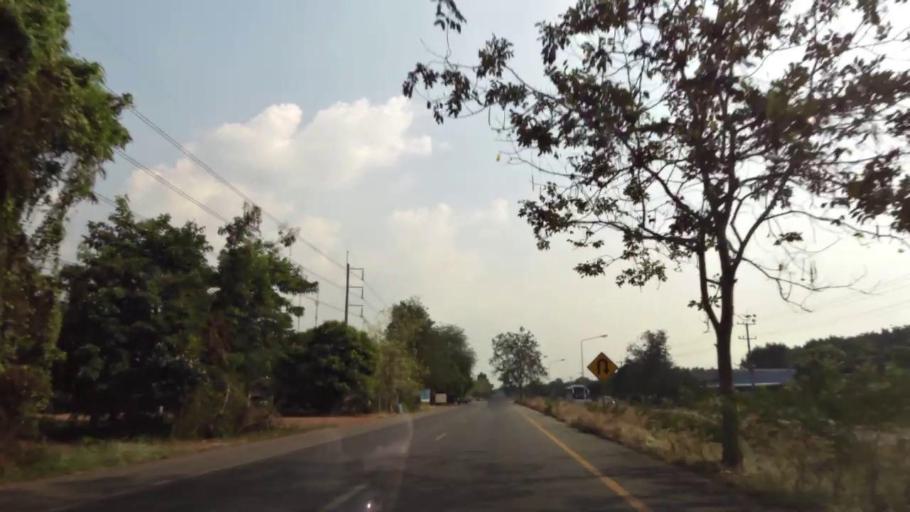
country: TH
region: Rayong
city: Wang Chan
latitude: 12.9042
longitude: 101.5392
